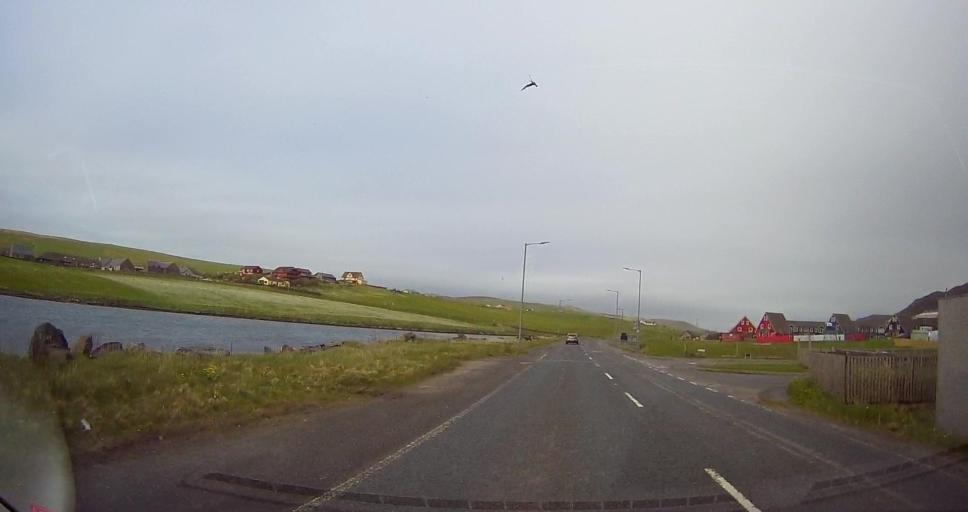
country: GB
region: Scotland
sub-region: Shetland Islands
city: Lerwick
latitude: 60.1386
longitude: -1.2667
